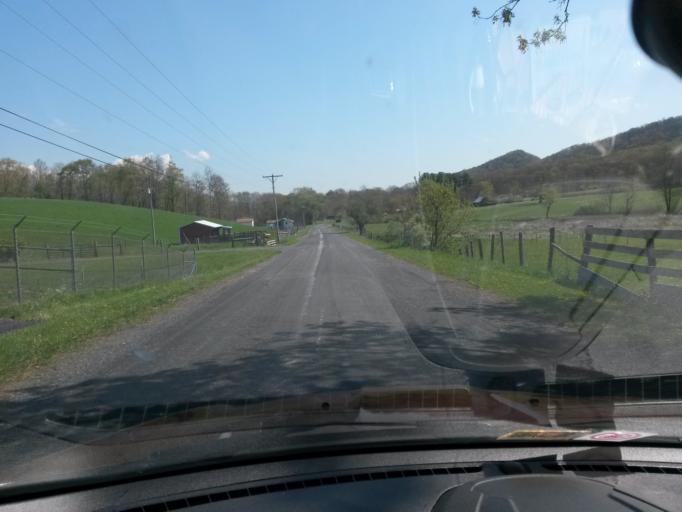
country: US
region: Virginia
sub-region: Highland County
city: Monterey
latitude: 38.4131
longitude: -79.5751
